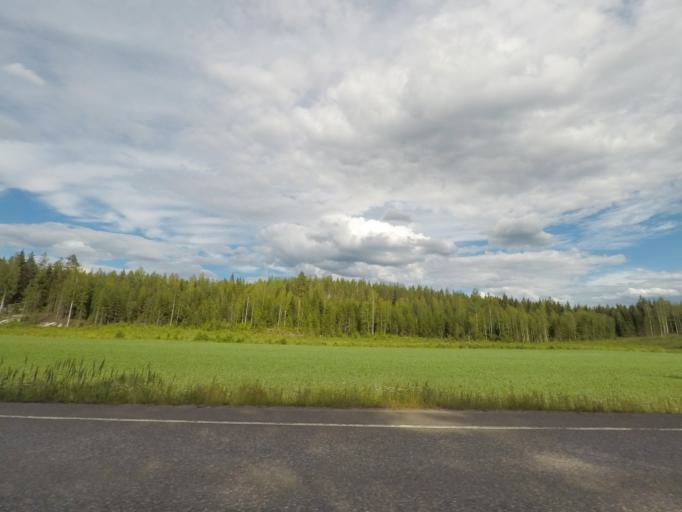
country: FI
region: Paijanne Tavastia
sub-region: Lahti
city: Hollola
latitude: 60.8401
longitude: 25.4939
